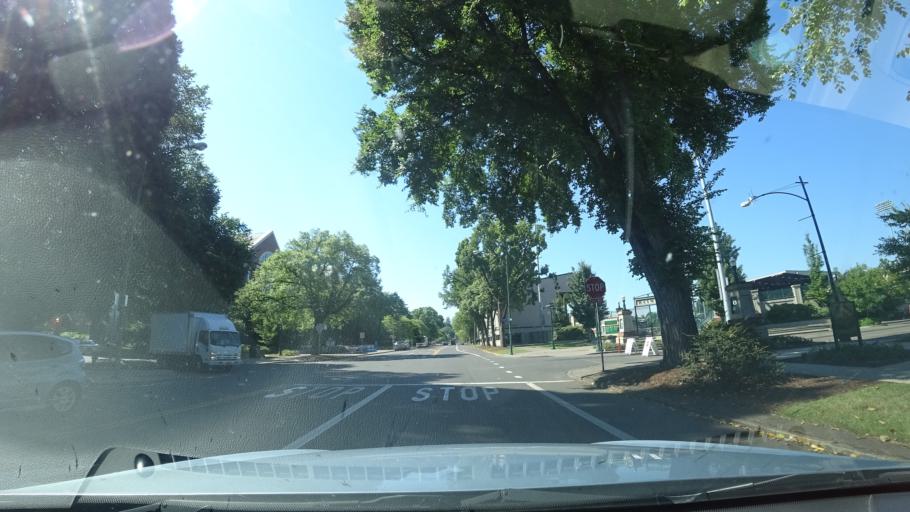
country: US
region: Oregon
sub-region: Lane County
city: Eugene
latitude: 44.0437
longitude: -123.0697
